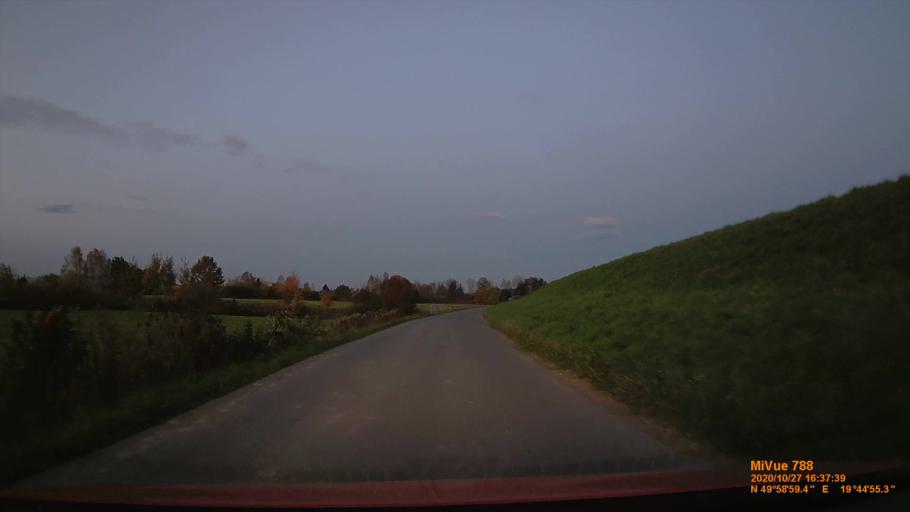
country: PL
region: Lesser Poland Voivodeship
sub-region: Powiat krakowski
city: Wolowice
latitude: 49.9831
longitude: 19.7488
